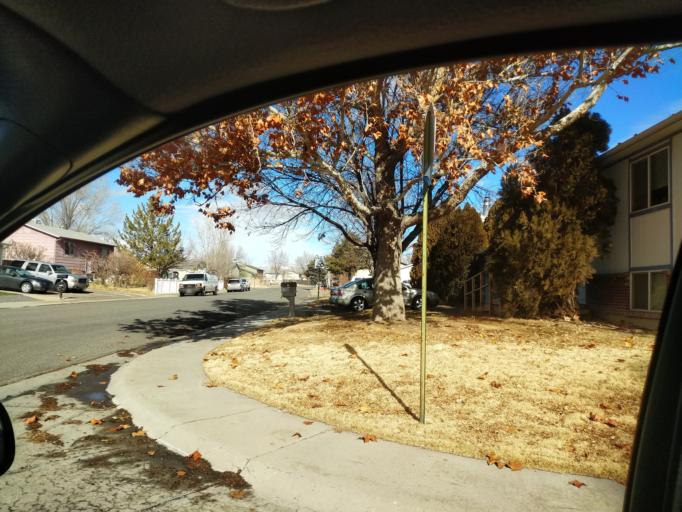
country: US
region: Colorado
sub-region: Mesa County
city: Fruitvale
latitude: 39.0741
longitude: -108.4877
